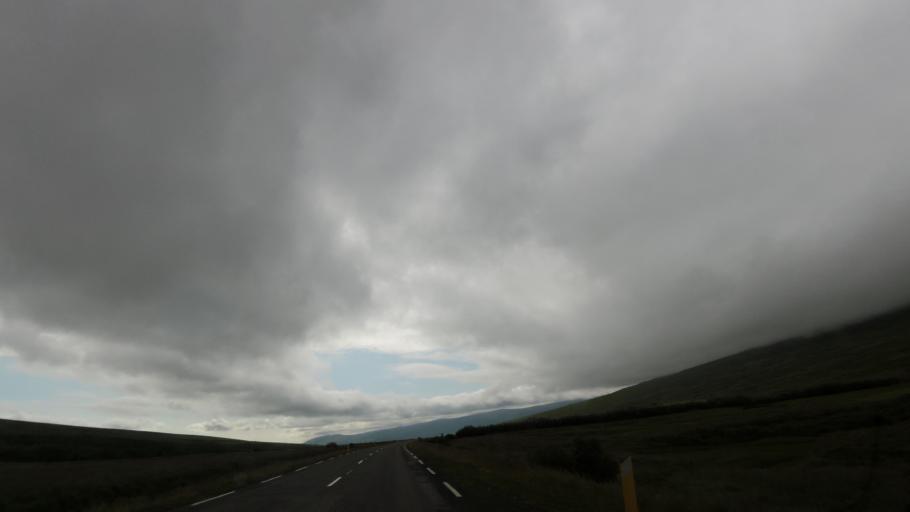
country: IS
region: Northeast
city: Laugar
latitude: 65.7603
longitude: -17.5830
